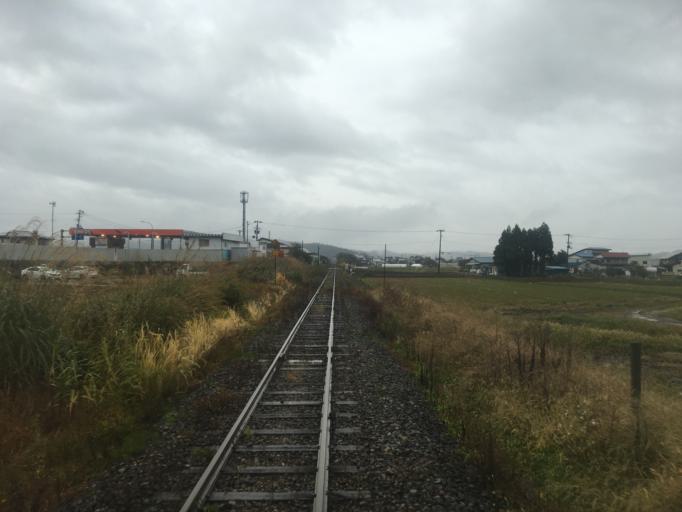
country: JP
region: Yamagata
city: Shinjo
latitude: 38.7659
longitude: 140.4688
